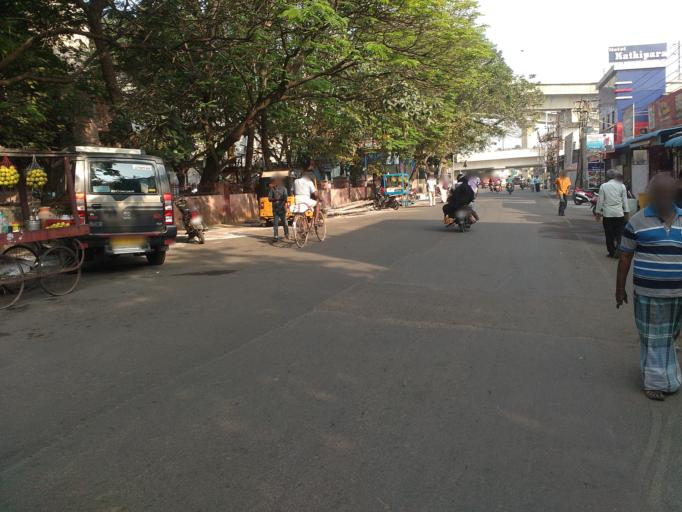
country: IN
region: Tamil Nadu
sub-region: Kancheepuram
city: Alandur
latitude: 13.0048
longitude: 80.2028
